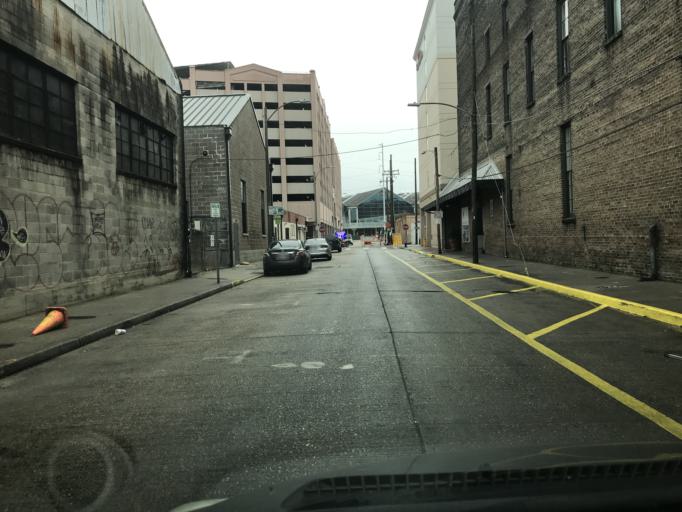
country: US
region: Louisiana
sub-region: Orleans Parish
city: New Orleans
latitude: 29.9420
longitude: -90.0666
